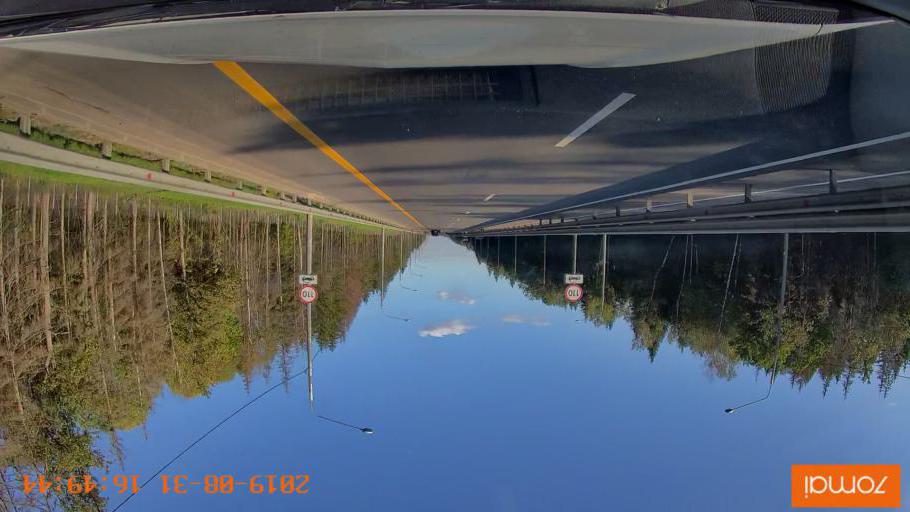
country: RU
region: Kaluga
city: Pyatovskiy
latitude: 54.6957
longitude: 36.1570
